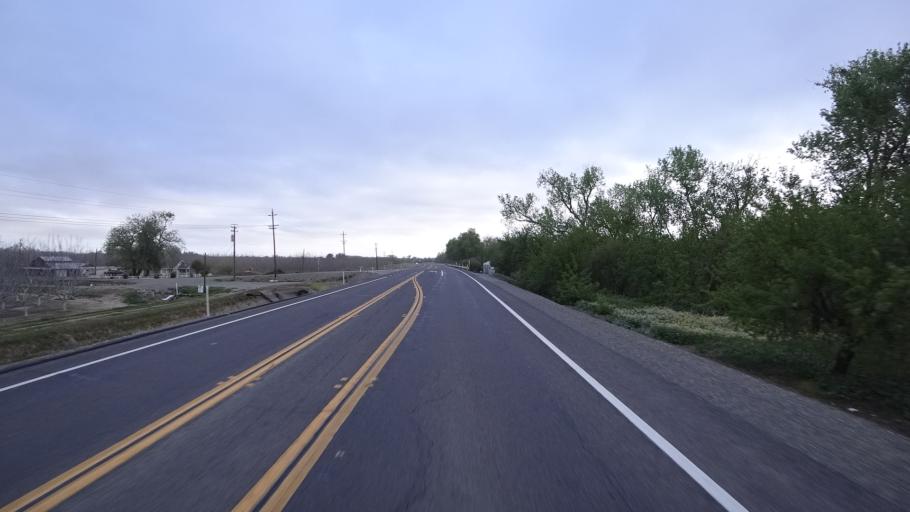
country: US
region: California
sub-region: Glenn County
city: Willows
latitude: 39.4273
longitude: -122.0112
